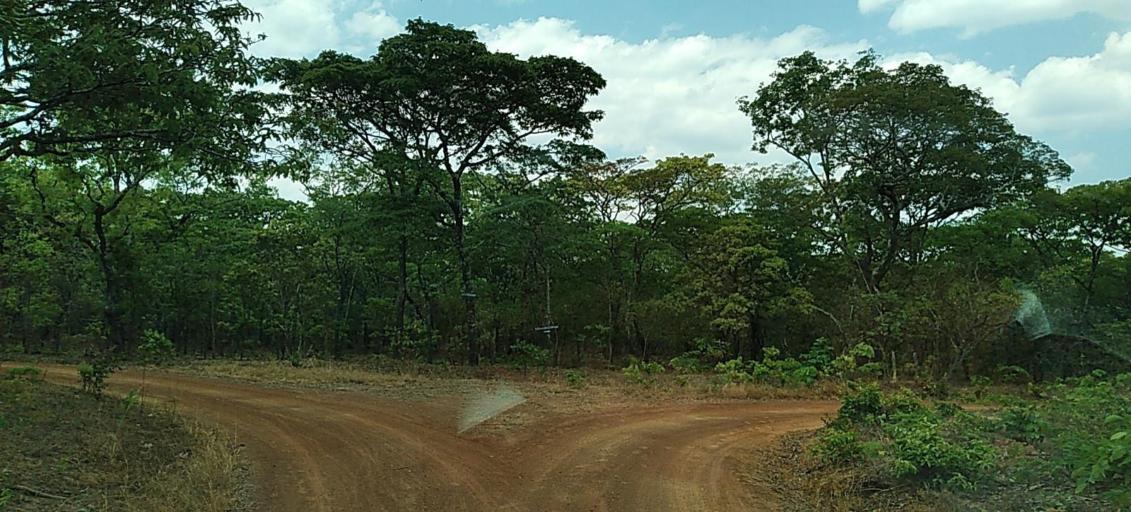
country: ZM
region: Copperbelt
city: Chililabombwe
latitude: -12.4597
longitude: 27.5945
